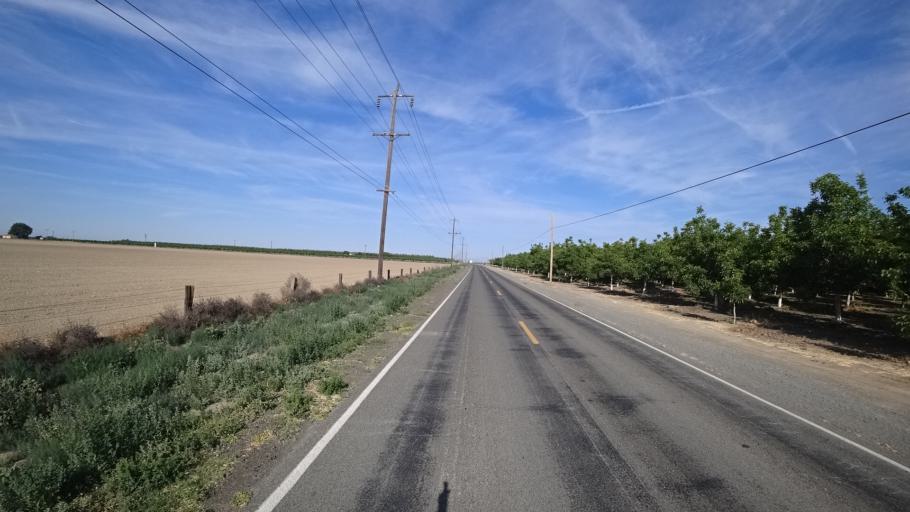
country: US
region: California
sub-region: Tulare County
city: Goshen
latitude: 36.3426
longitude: -119.4899
